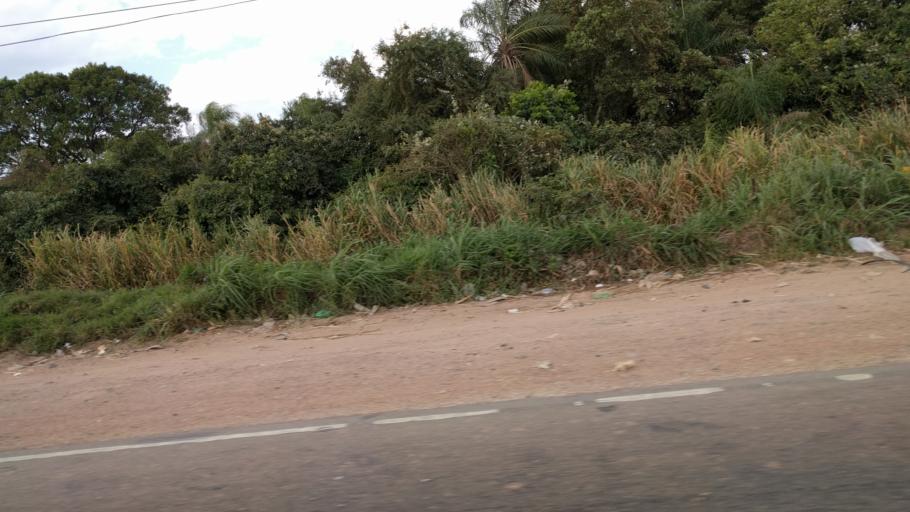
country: BO
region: Santa Cruz
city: Warnes
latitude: -17.5359
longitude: -63.1611
